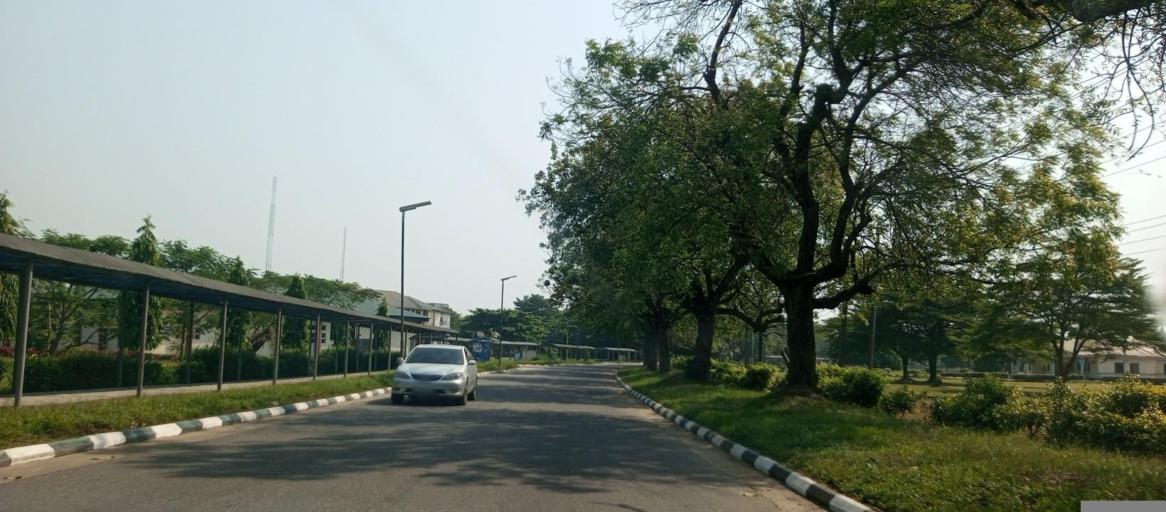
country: NG
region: Rivers
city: Emuoha
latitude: 4.9044
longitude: 6.9156
